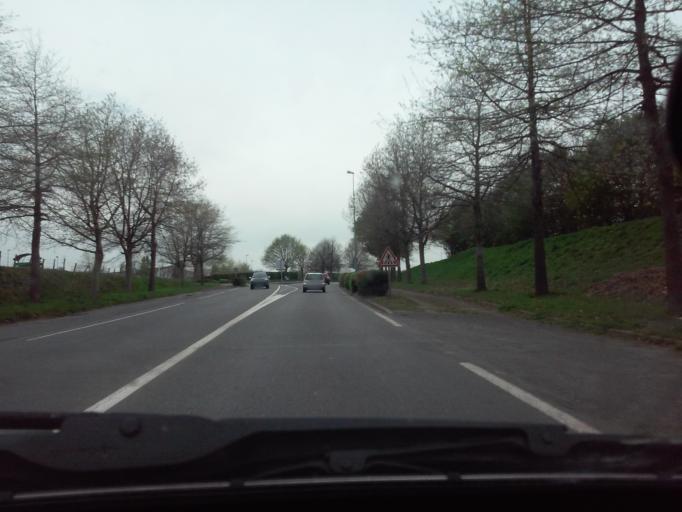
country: FR
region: Brittany
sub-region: Departement d'Ille-et-Vilaine
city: Lecousse
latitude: 48.3503
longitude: -1.2293
